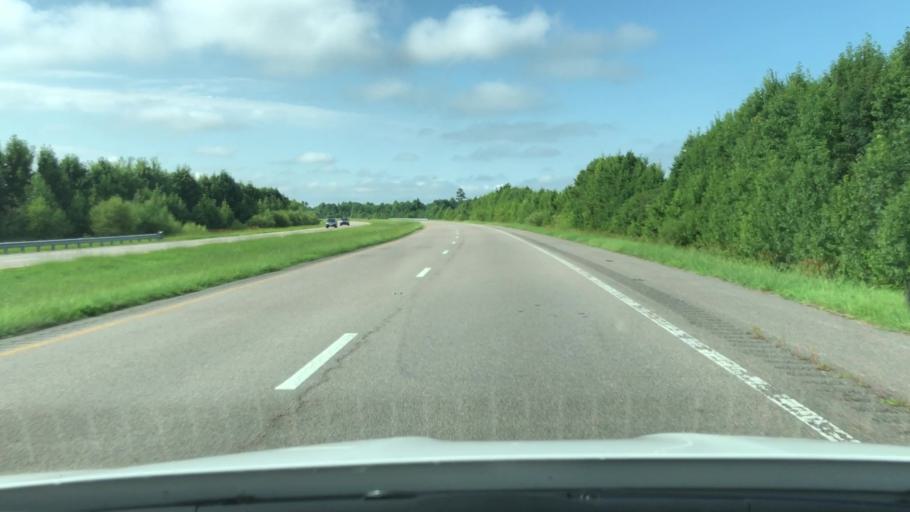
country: US
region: Virginia
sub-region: City of Portsmouth
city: Portsmouth Heights
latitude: 36.6056
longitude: -76.3800
